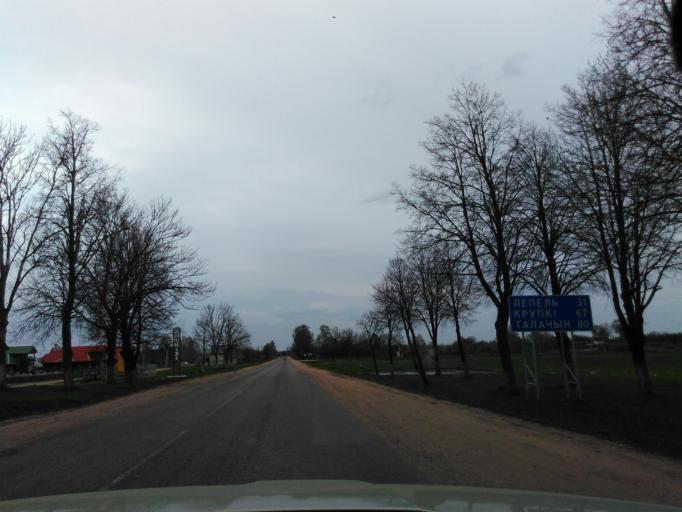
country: BY
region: Vitebsk
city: Chashniki
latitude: 54.8418
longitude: 29.1487
